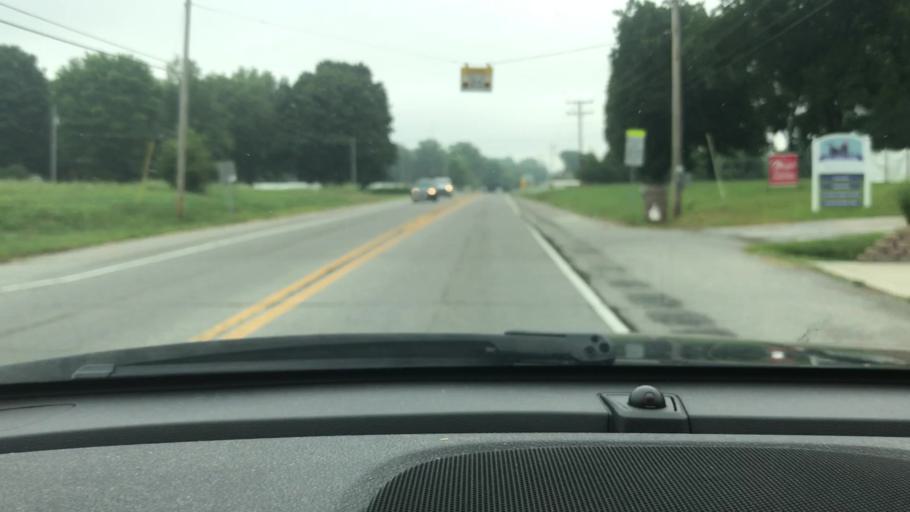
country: US
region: Tennessee
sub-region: Sumner County
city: White House
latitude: 36.4310
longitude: -86.6885
